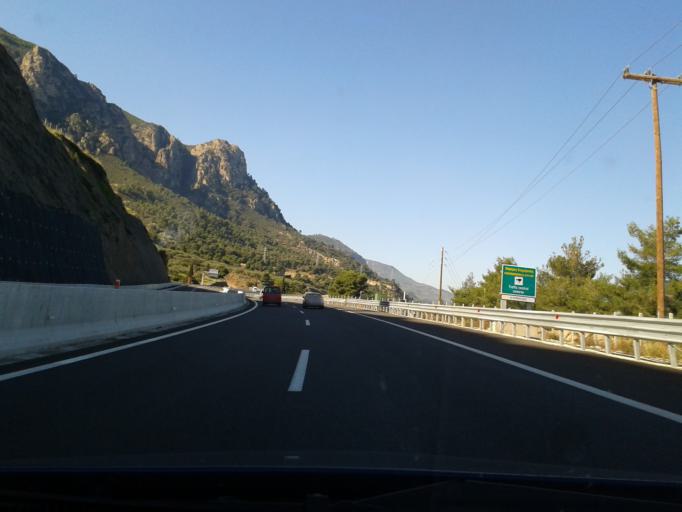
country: GR
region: West Greece
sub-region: Nomos Achaias
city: Akrata
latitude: 38.1757
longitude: 22.2265
